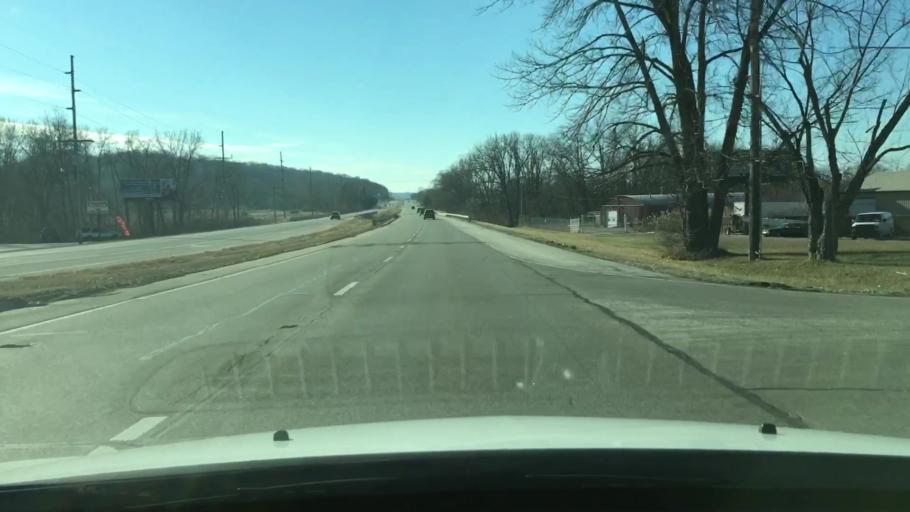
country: US
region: Illinois
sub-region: Woodford County
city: Germantown Hills
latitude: 40.7399
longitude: -89.5148
